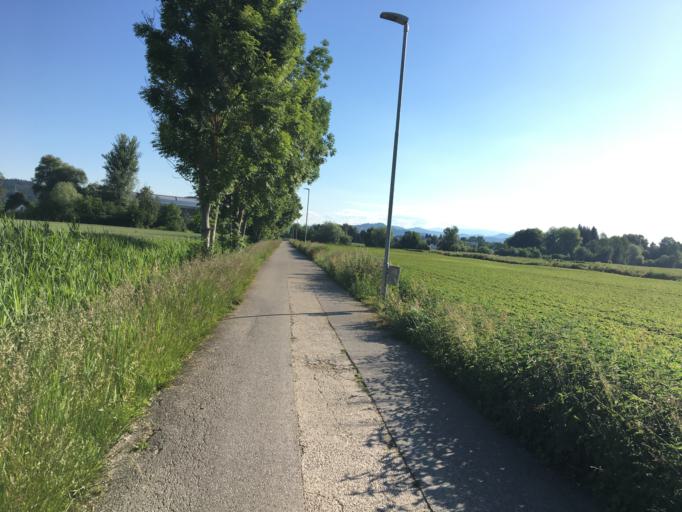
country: AT
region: Carinthia
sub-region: Klagenfurt am Woerthersee
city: Klagenfurt am Woerthersee
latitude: 46.6030
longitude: 14.2762
